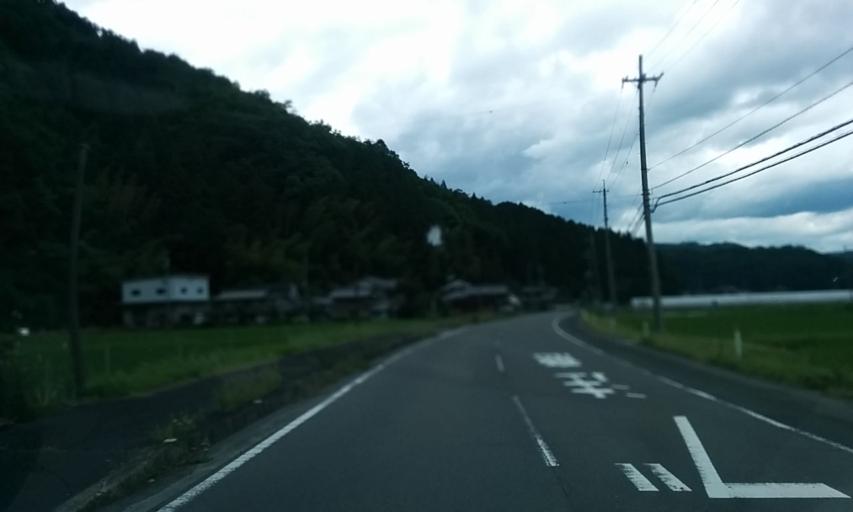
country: JP
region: Kyoto
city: Kameoka
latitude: 35.0972
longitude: 135.4325
